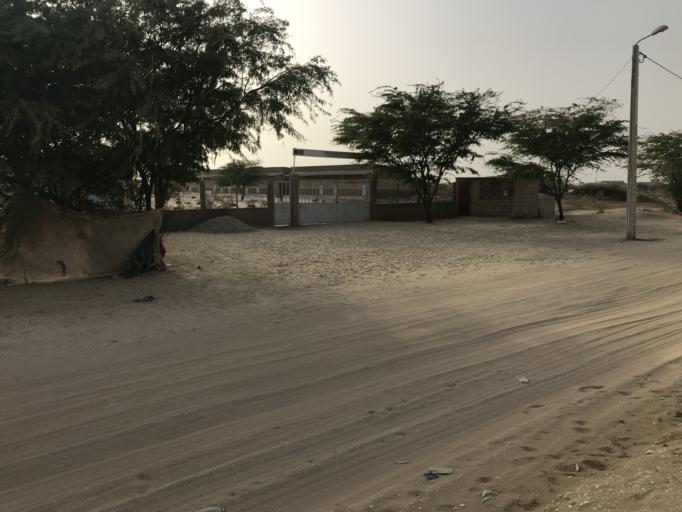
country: SN
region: Saint-Louis
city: Saint-Louis
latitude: 16.0253
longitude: -16.4458
